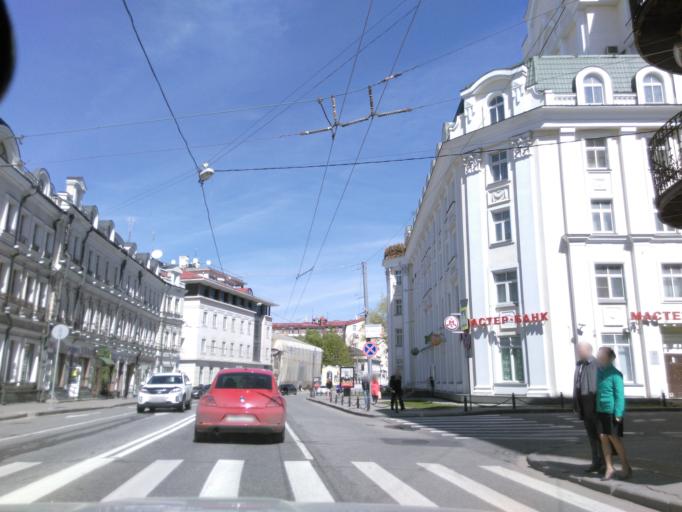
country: RU
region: Moscow
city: Moscow
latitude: 55.7394
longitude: 37.5962
